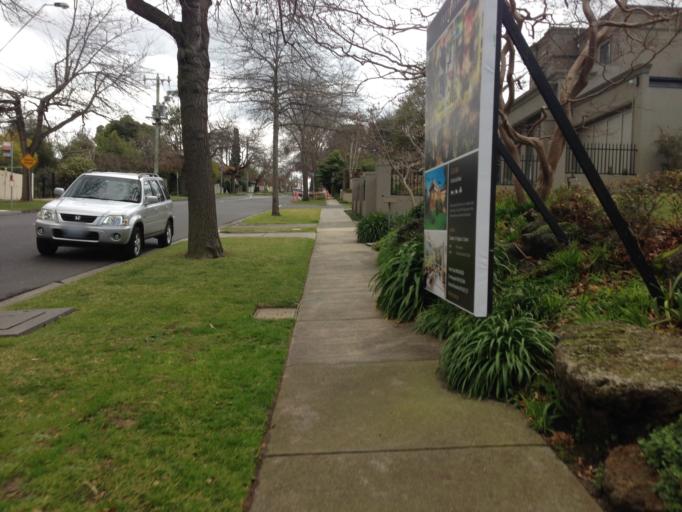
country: AU
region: Victoria
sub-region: Boroondara
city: Camberwell
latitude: -37.8511
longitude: 145.0680
